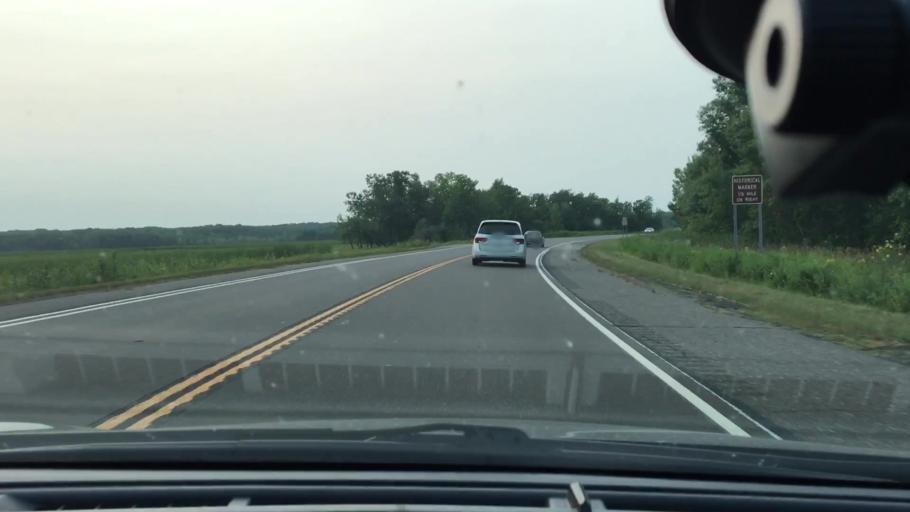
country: US
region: Minnesota
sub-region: Mille Lacs County
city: Vineland
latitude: 46.1550
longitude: -93.7538
